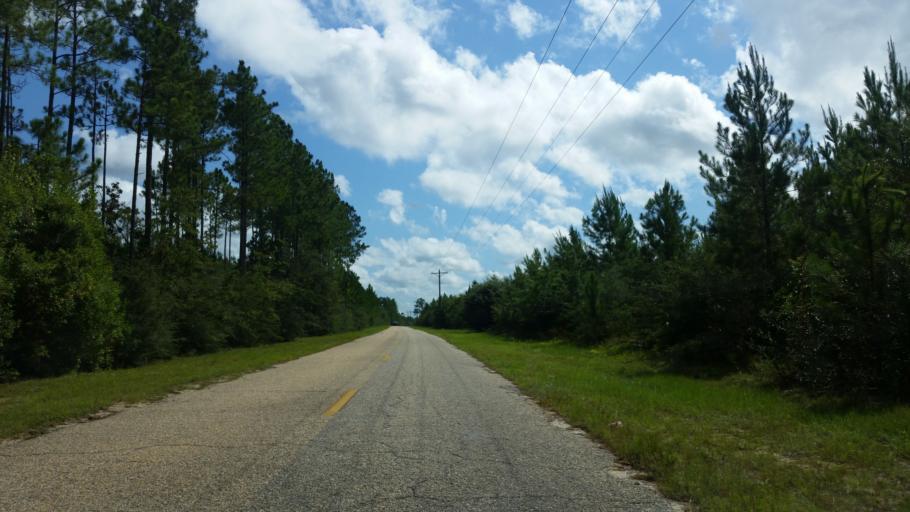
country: US
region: Florida
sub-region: Santa Rosa County
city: Point Baker
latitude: 30.7212
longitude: -86.9129
